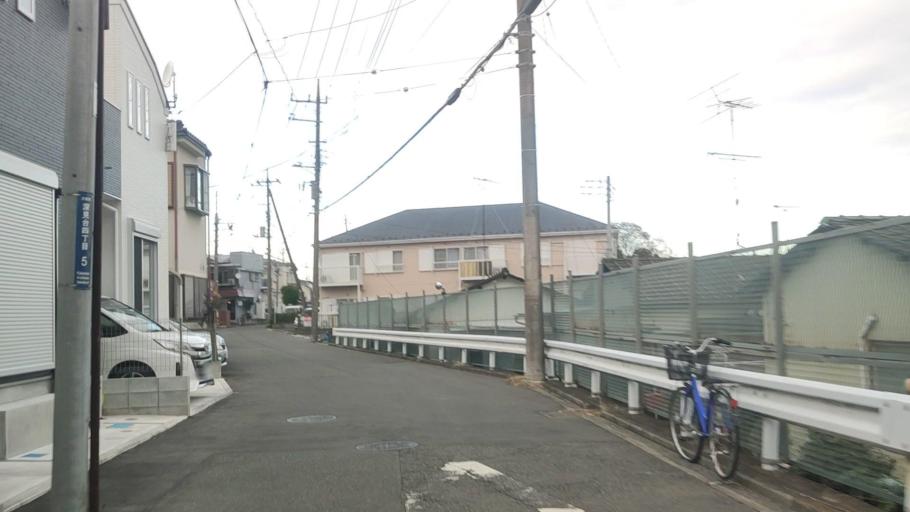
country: JP
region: Kanagawa
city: Minami-rinkan
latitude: 35.4719
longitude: 139.4683
